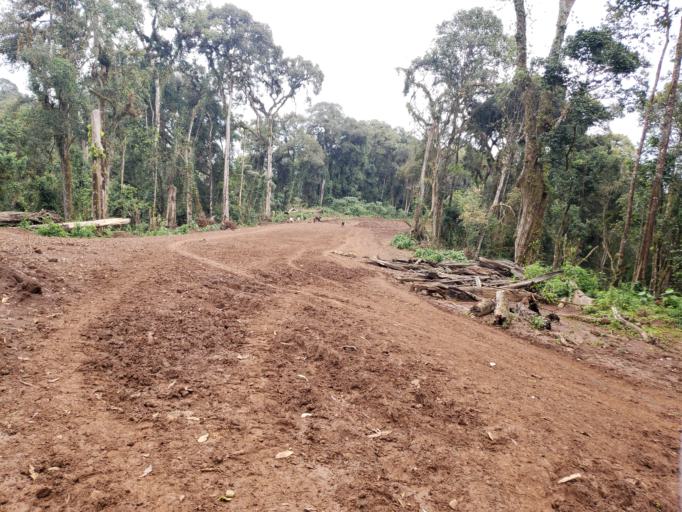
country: ET
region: Oromiya
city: Dodola
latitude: 6.5857
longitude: 39.4141
